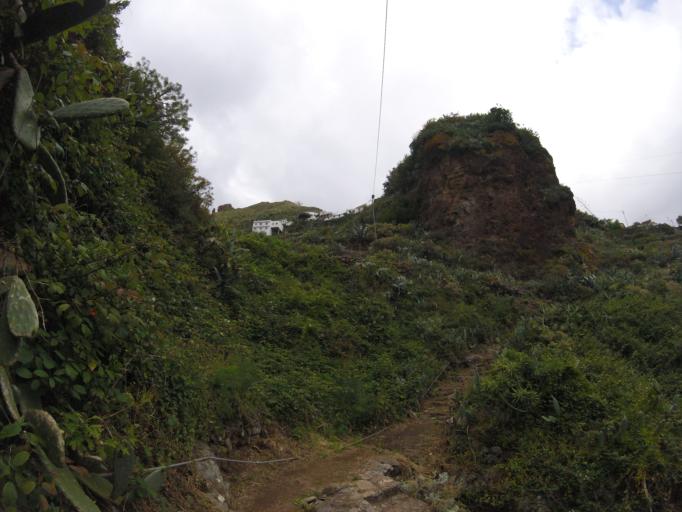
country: ES
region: Canary Islands
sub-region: Provincia de Santa Cruz de Tenerife
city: Tegueste
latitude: 28.5471
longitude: -16.2952
